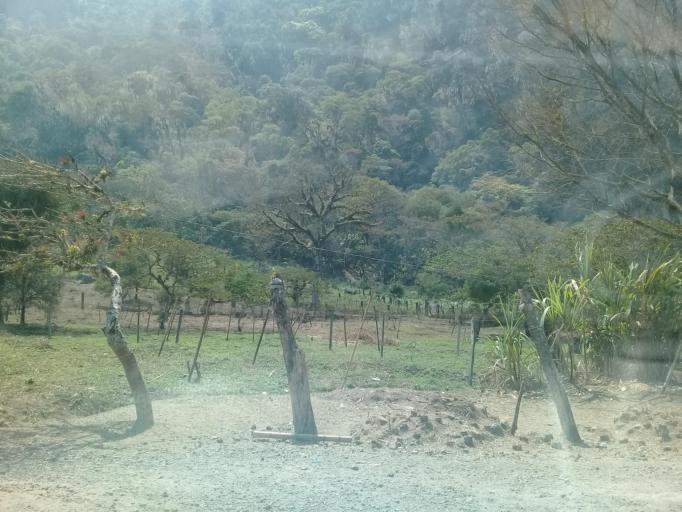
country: MX
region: Veracruz
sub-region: Ixtaczoquitlan
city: Capoluca
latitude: 18.8002
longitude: -96.9924
